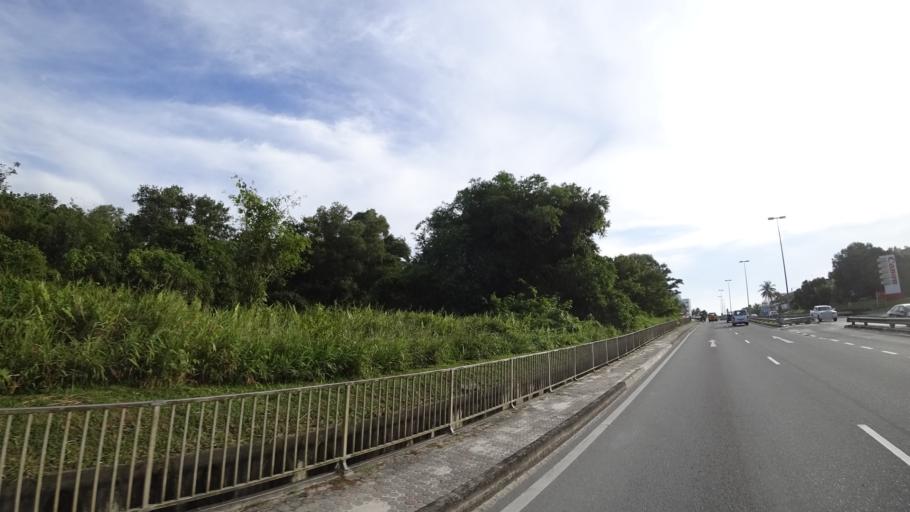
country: BN
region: Brunei and Muara
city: Bandar Seri Begawan
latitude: 4.8598
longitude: 114.8964
